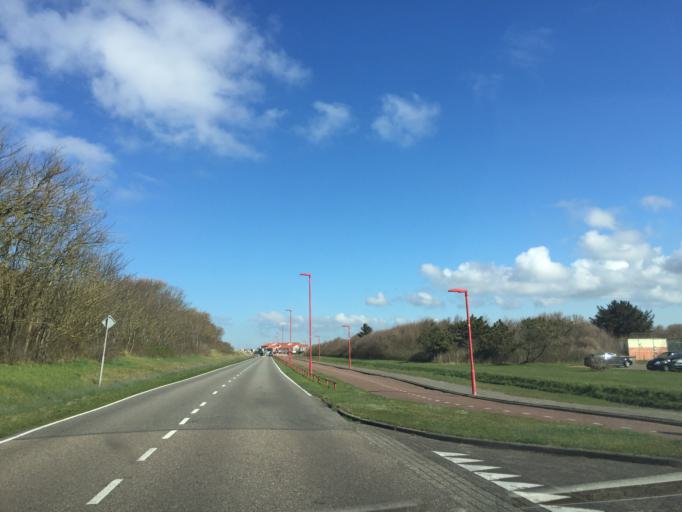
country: NL
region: North Holland
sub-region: Gemeente Den Helder
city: Den Helder
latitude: 52.9030
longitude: 4.7183
